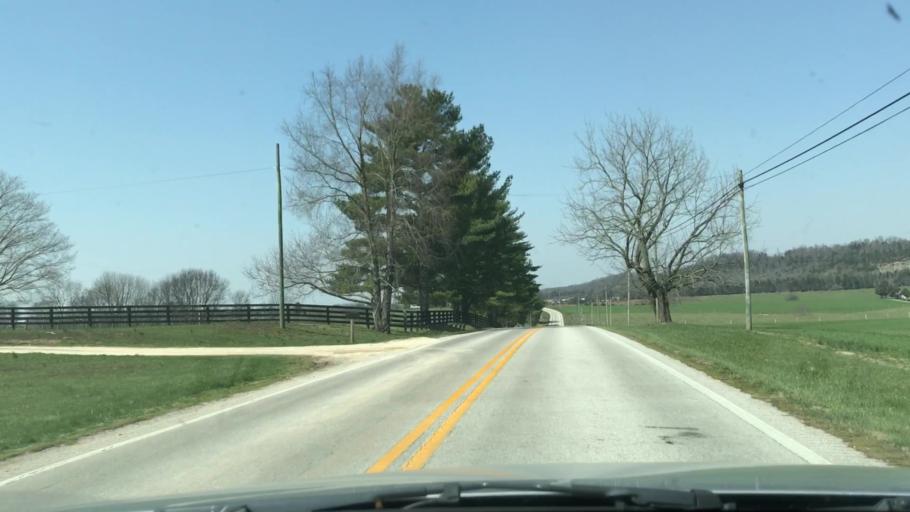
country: US
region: Kentucky
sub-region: Barren County
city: Cave City
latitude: 37.0931
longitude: -86.1043
